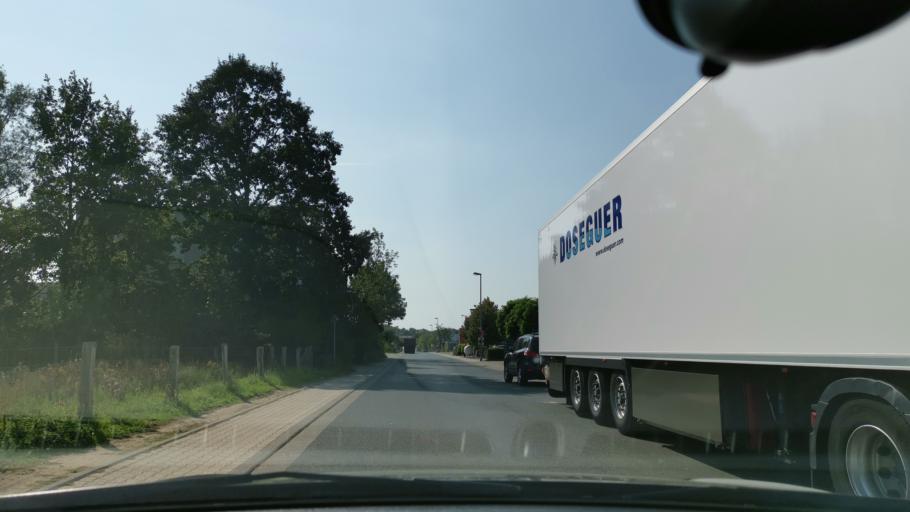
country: DE
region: North Rhine-Westphalia
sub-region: Regierungsbezirk Dusseldorf
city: Juchen
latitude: 51.1003
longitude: 6.5263
